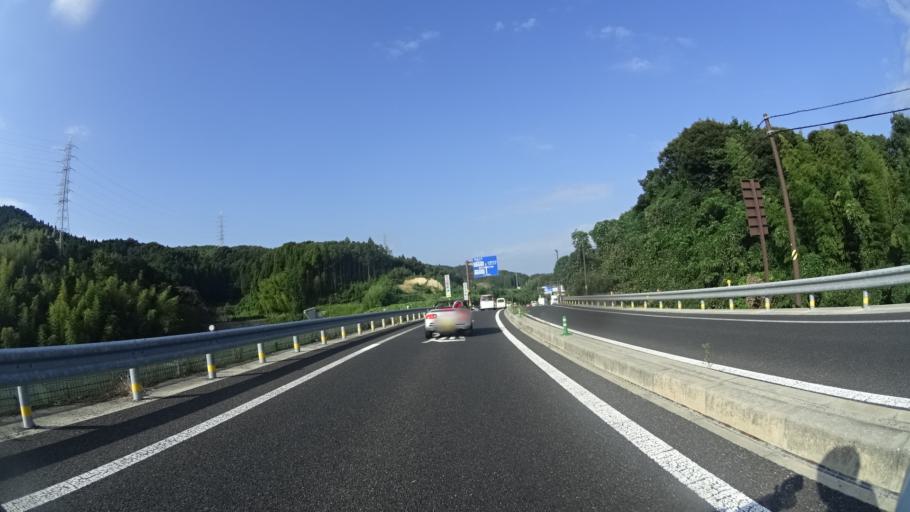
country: JP
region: Shimane
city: Izumo
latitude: 35.3262
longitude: 132.7135
